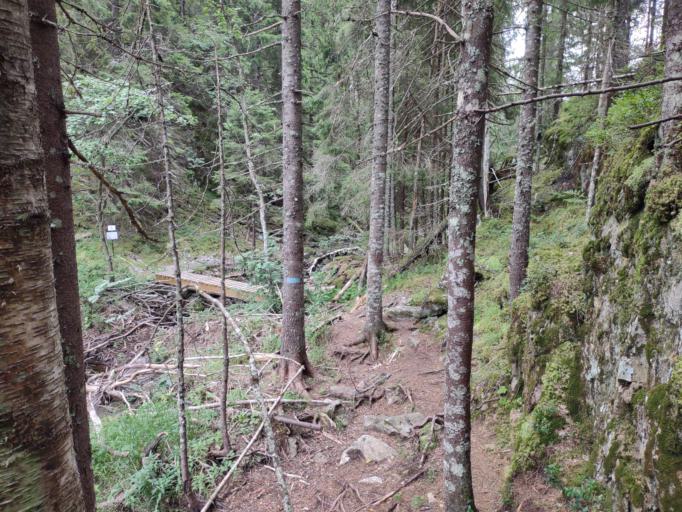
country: NO
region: Akershus
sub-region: Enebakk
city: Flateby
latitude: 59.8184
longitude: 11.0497
